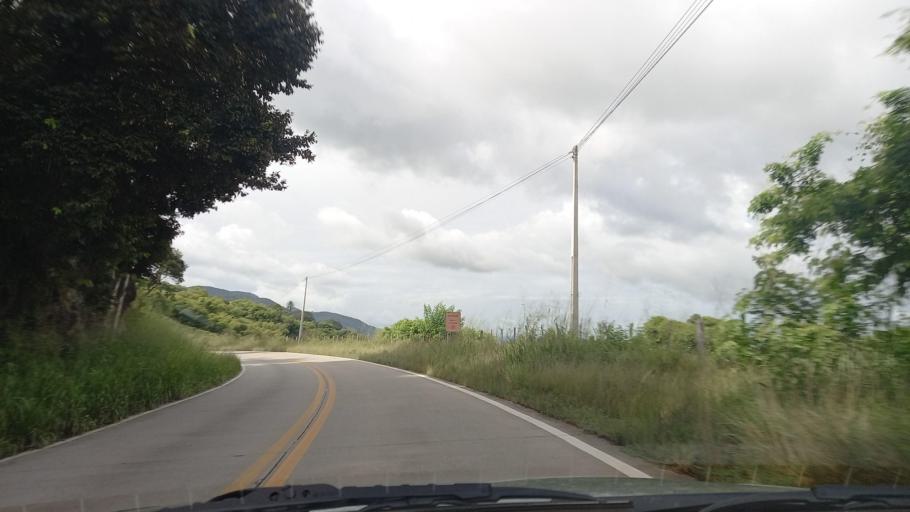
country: BR
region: Pernambuco
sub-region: Maraial
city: Maraial
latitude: -8.7870
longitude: -35.8782
